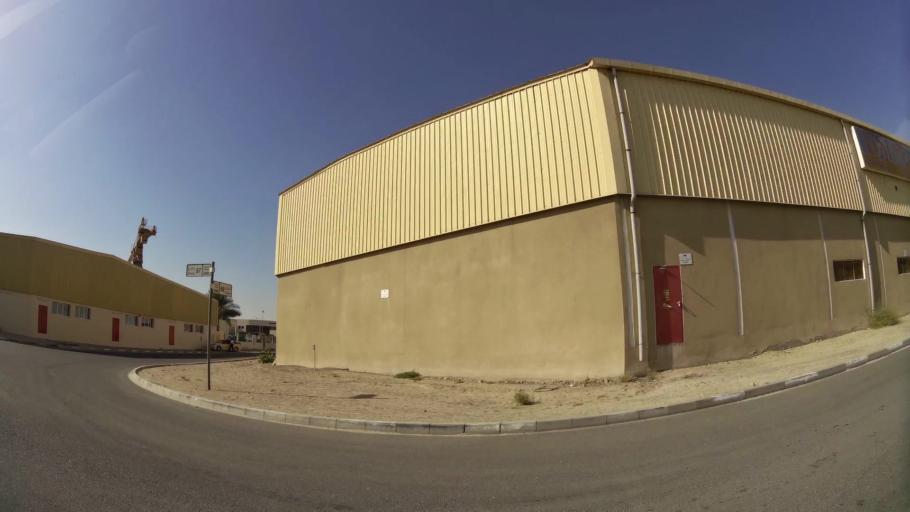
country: AE
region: Dubai
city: Dubai
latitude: 24.9842
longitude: 55.1144
